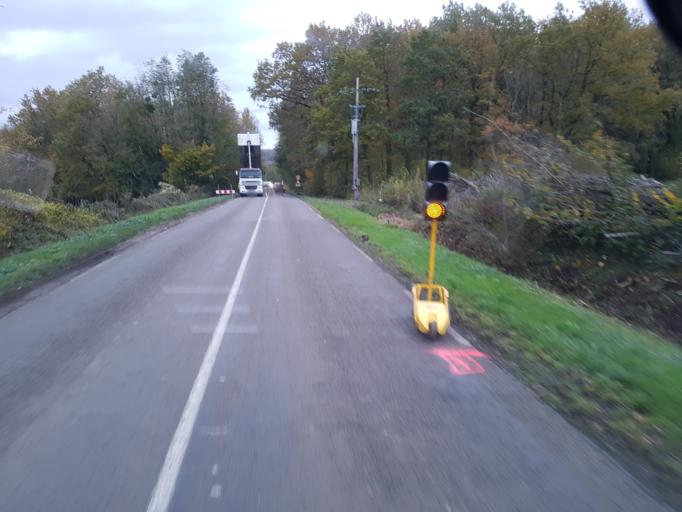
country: FR
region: Picardie
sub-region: Departement de l'Aisne
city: Nesles-la-Montagne
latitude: 49.0105
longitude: 3.4202
